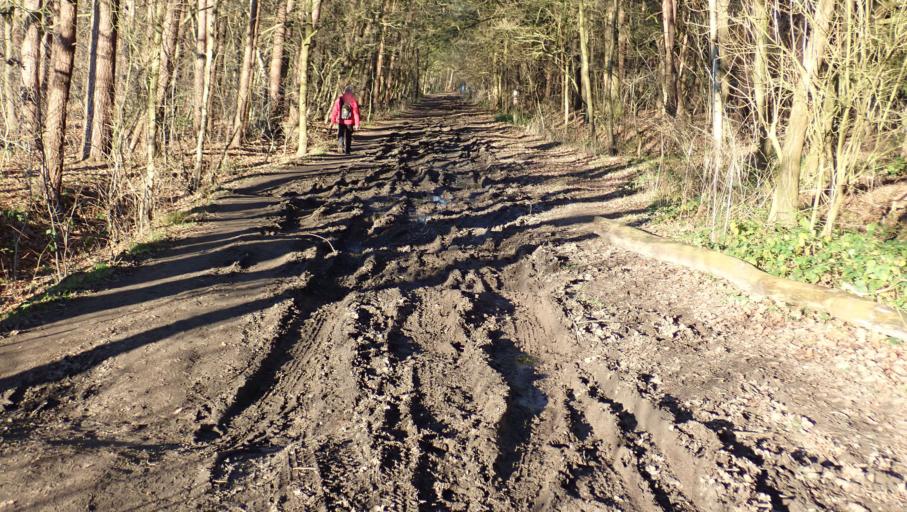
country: BE
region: Flanders
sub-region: Provincie Antwerpen
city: Schilde
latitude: 51.2247
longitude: 4.6177
